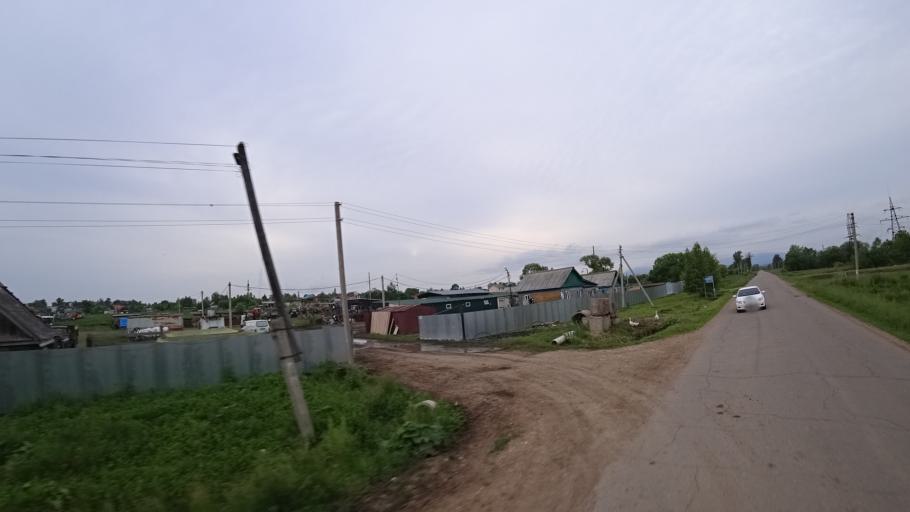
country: RU
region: Primorskiy
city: Novosysoyevka
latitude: 44.2323
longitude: 133.3711
